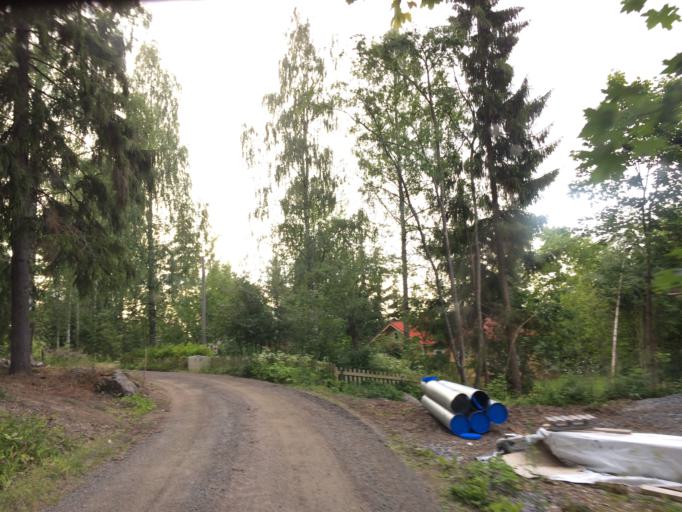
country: FI
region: Haeme
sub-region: Haemeenlinna
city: Tervakoski
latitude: 60.8556
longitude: 24.6232
